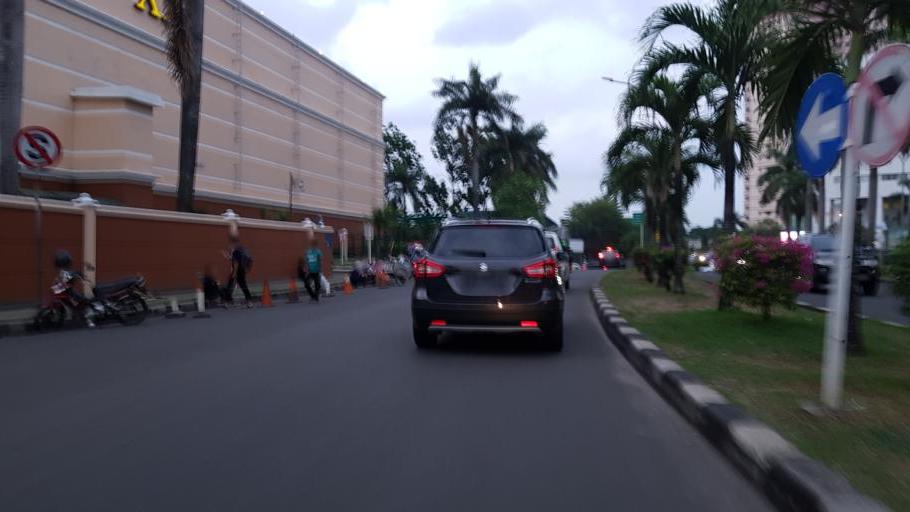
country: ID
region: West Java
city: Ciputat
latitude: -6.1878
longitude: 106.7350
